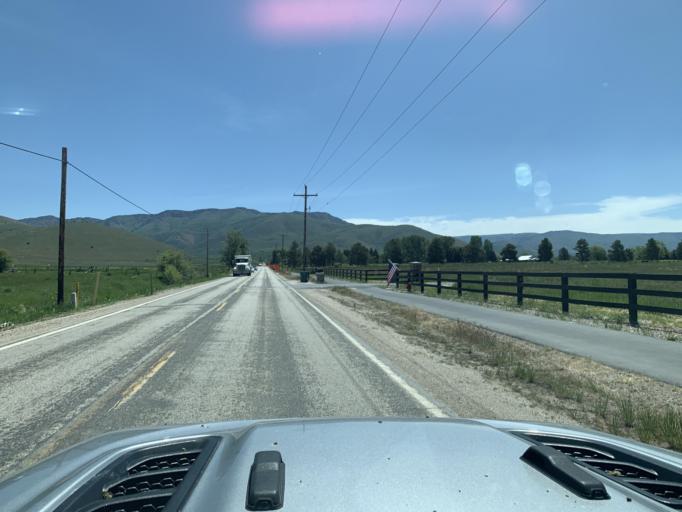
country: US
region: Utah
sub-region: Weber County
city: Wolf Creek
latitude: 41.2932
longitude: -111.7849
